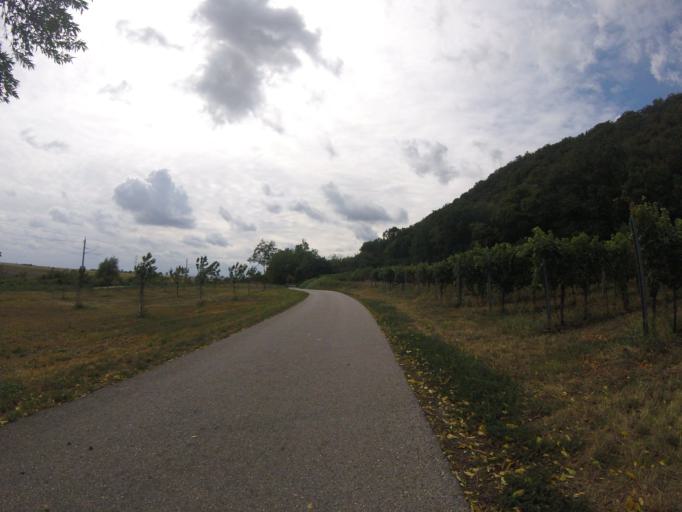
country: AT
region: Burgenland
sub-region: Politischer Bezirk Neusiedl am See
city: Jois
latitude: 47.9528
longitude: 16.7765
